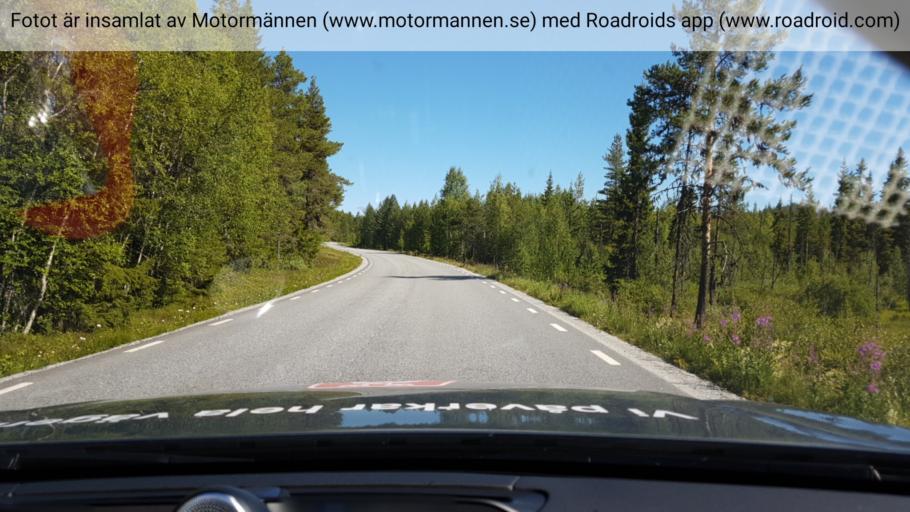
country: SE
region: Jaemtland
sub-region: Braecke Kommun
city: Braecke
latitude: 63.0970
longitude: 15.4431
